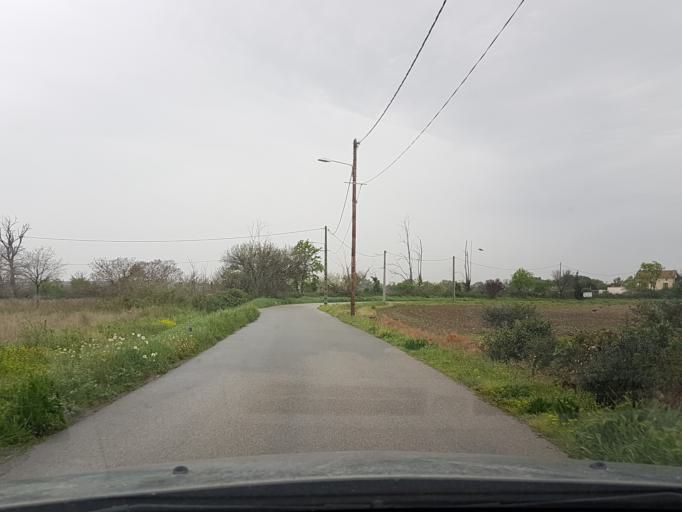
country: FR
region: Provence-Alpes-Cote d'Azur
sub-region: Departement du Vaucluse
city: Le Pontet
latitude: 43.9814
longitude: 4.8711
